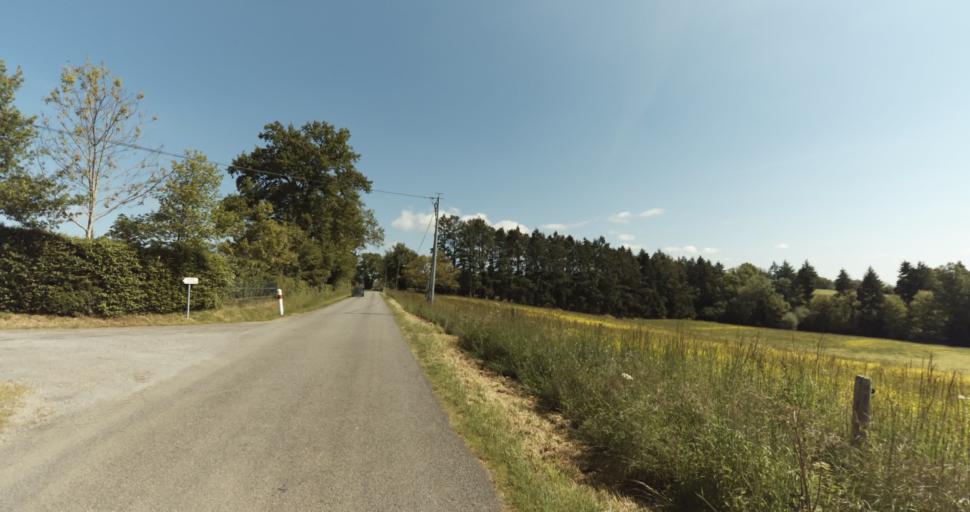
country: FR
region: Limousin
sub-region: Departement de la Haute-Vienne
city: Le Vigen
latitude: 45.7299
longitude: 1.2878
